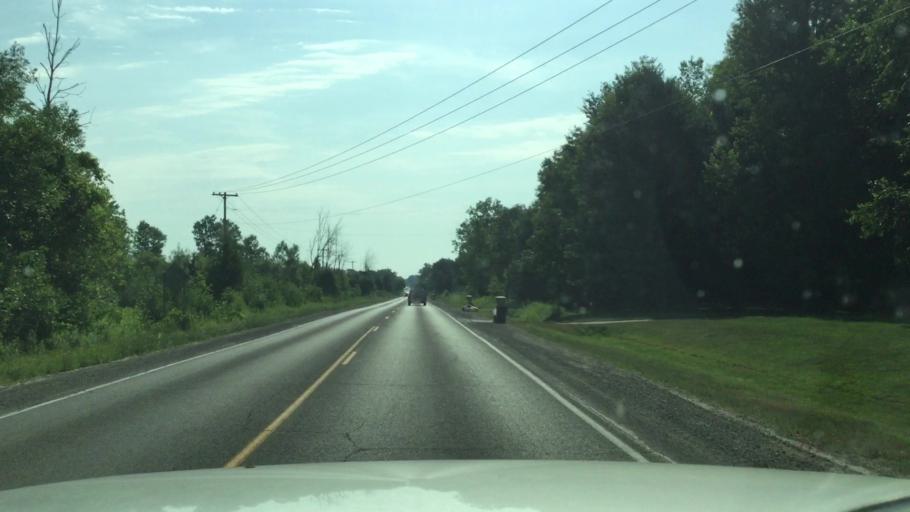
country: US
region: Michigan
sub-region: Genesee County
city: Flushing
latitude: 43.1177
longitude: -83.8701
